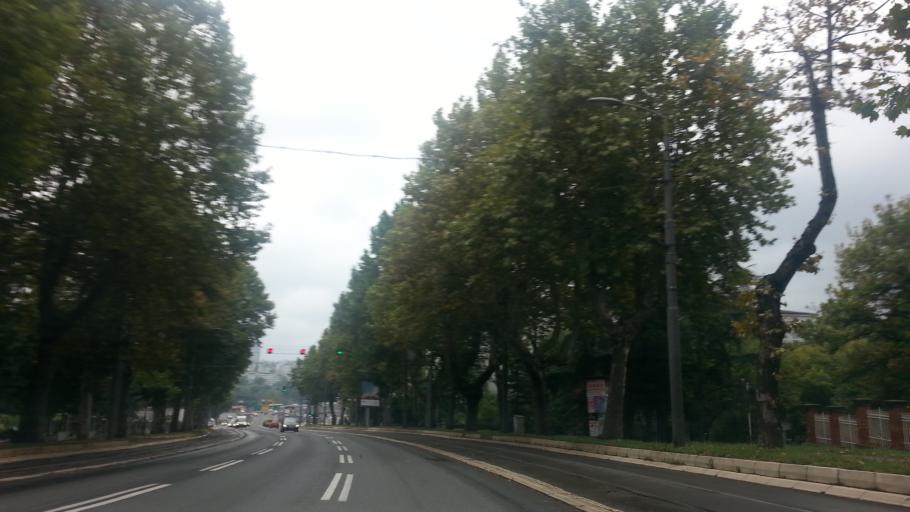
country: RS
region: Central Serbia
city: Belgrade
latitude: 44.7956
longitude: 20.4652
